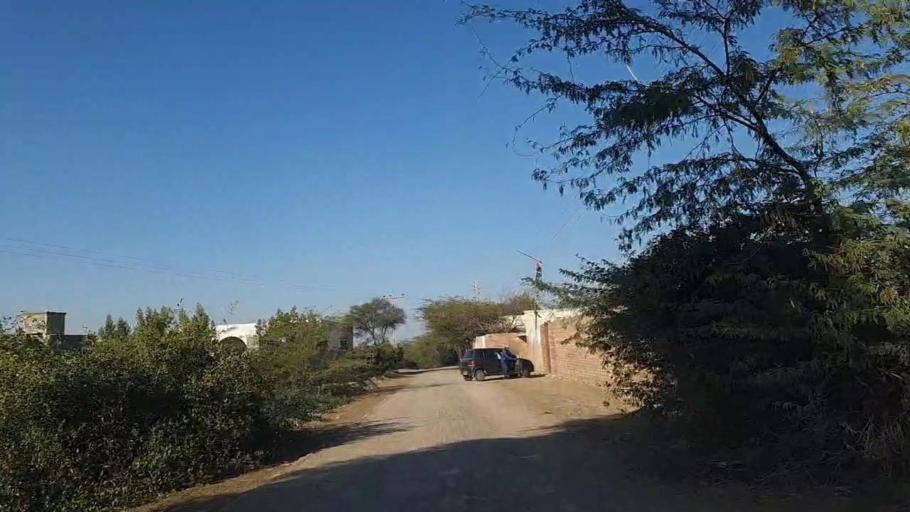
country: PK
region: Sindh
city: Naukot
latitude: 24.9850
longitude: 69.3646
